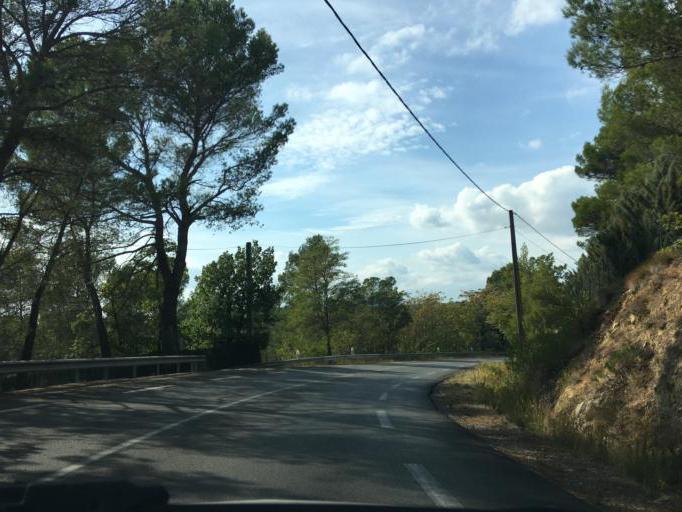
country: FR
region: Provence-Alpes-Cote d'Azur
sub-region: Departement du Var
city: Flayosc
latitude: 43.5414
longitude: 6.3638
